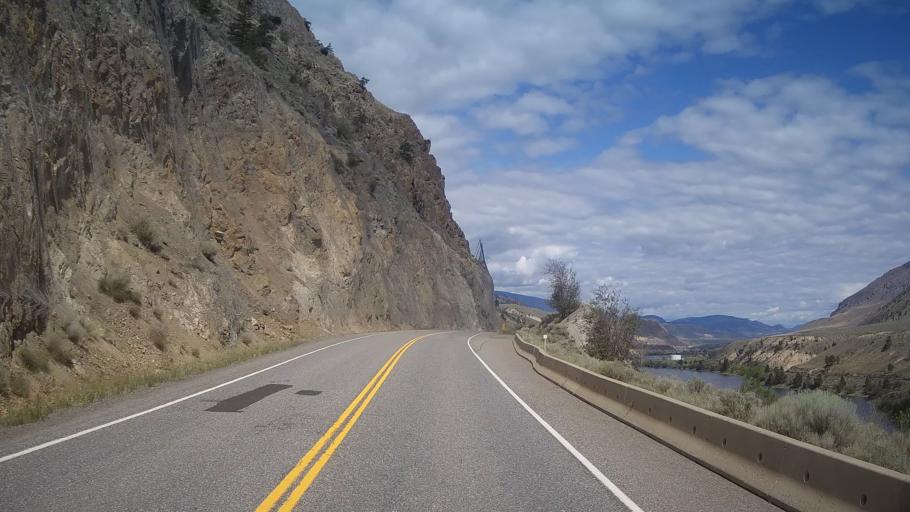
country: CA
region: British Columbia
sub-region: Thompson-Nicola Regional District
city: Ashcroft
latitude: 50.5386
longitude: -121.2874
